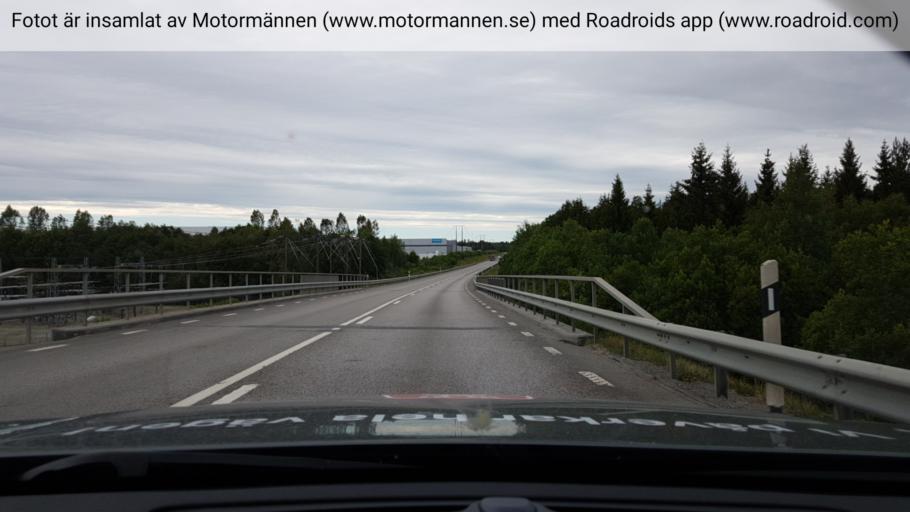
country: SE
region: Stockholm
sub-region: Haninge Kommun
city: Jordbro
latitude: 59.1545
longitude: 18.1268
